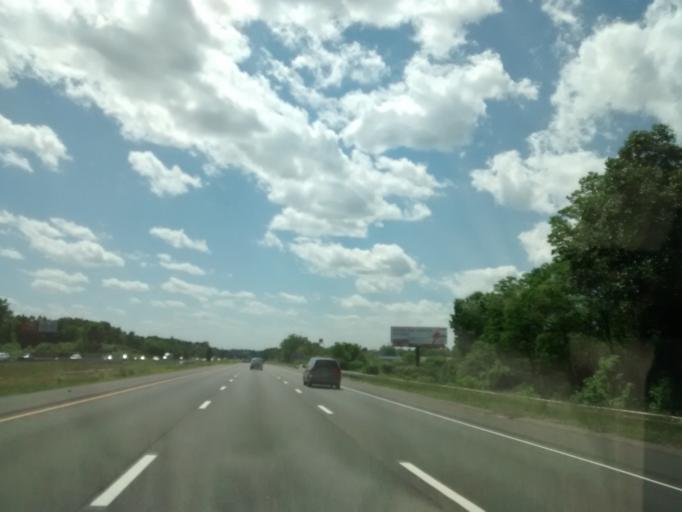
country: US
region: Connecticut
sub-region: Tolland County
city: Rockville
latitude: 41.8300
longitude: -72.4734
